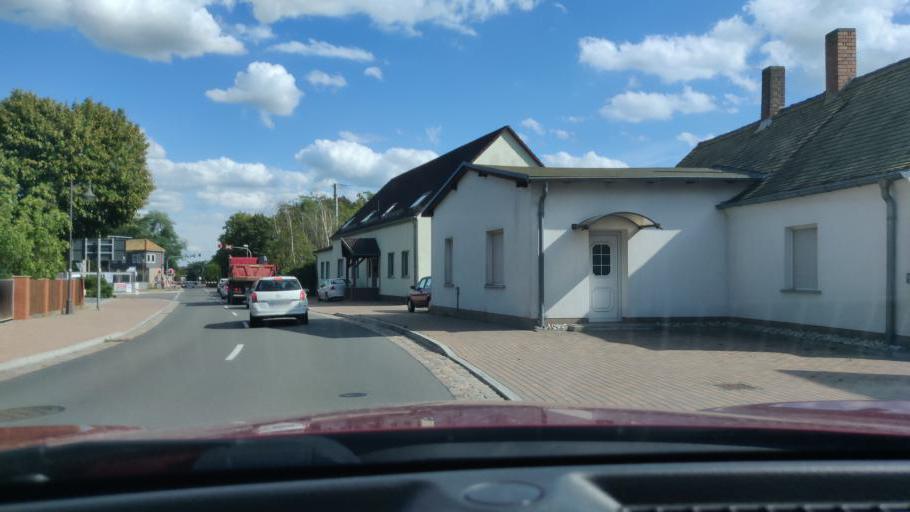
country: DE
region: Saxony
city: Mockrehna
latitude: 51.5052
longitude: 12.8150
